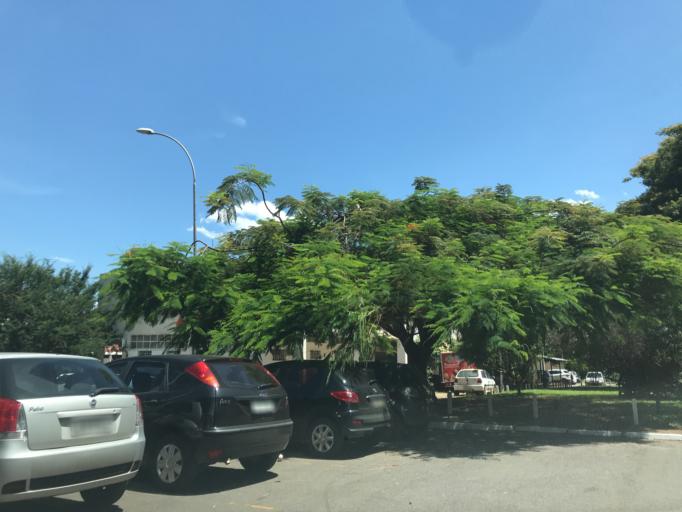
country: BR
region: Federal District
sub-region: Brasilia
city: Brasilia
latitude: -15.7783
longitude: -47.8889
